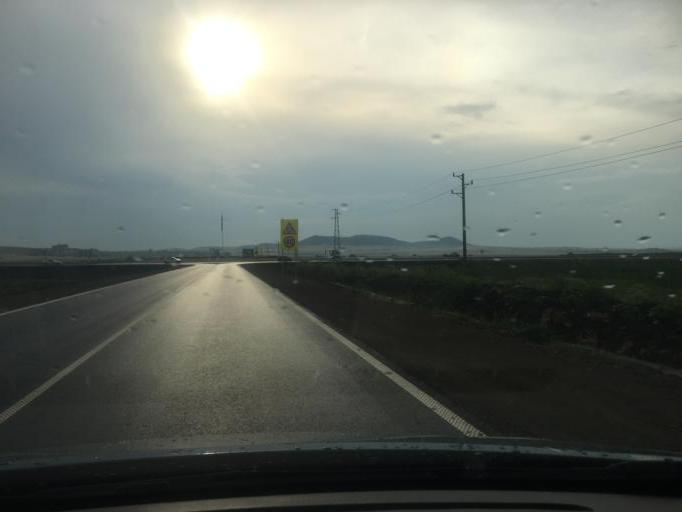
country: BG
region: Burgas
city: Aheloy
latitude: 42.6453
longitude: 27.6387
